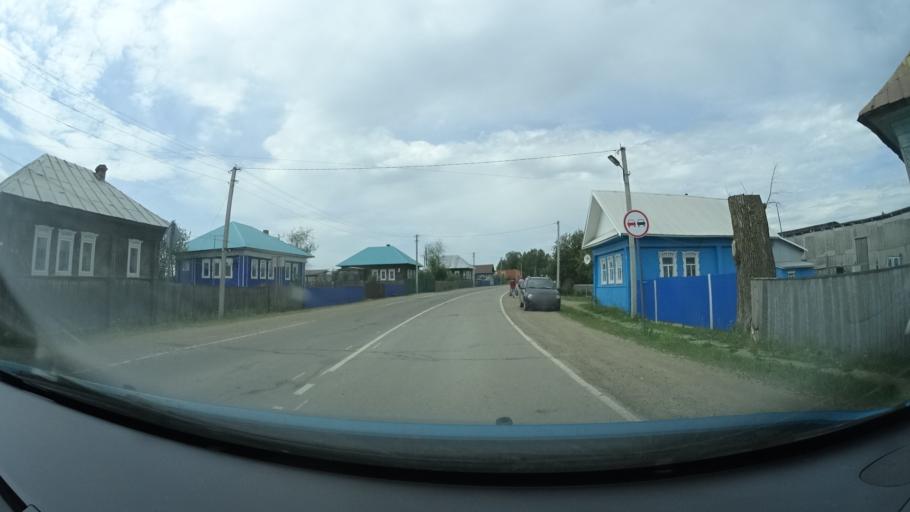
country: RU
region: Perm
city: Barda
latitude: 56.8236
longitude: 55.6296
